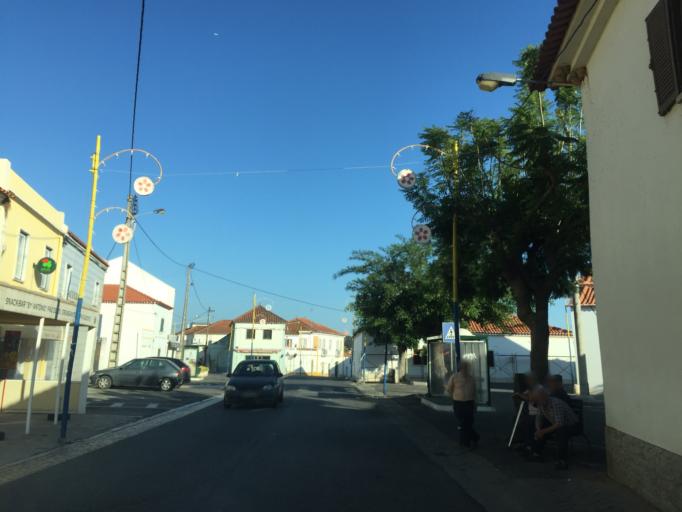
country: PT
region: Lisbon
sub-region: Alenquer
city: Alenquer
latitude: 39.1102
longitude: -8.9899
